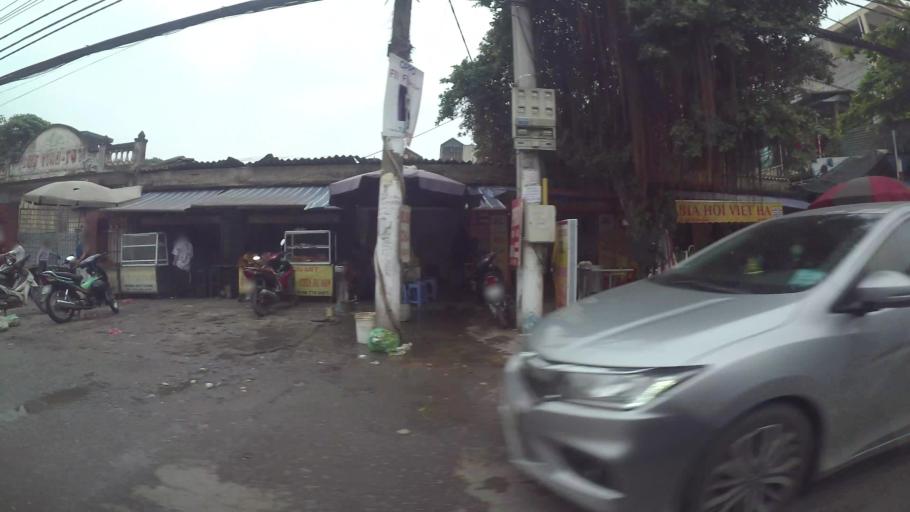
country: VN
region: Ha Noi
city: Hai BaTrung
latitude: 20.9836
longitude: 105.8755
